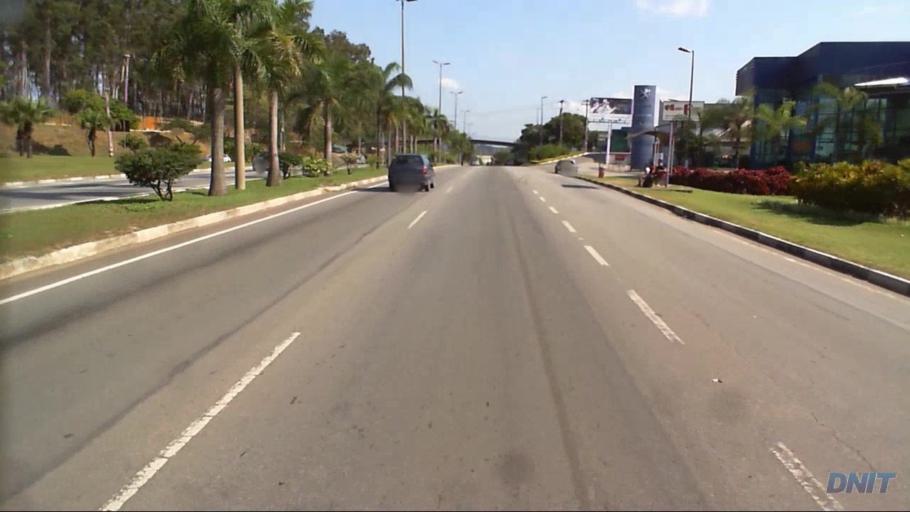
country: BR
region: Minas Gerais
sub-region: Ipatinga
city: Ipatinga
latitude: -19.4746
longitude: -42.5424
